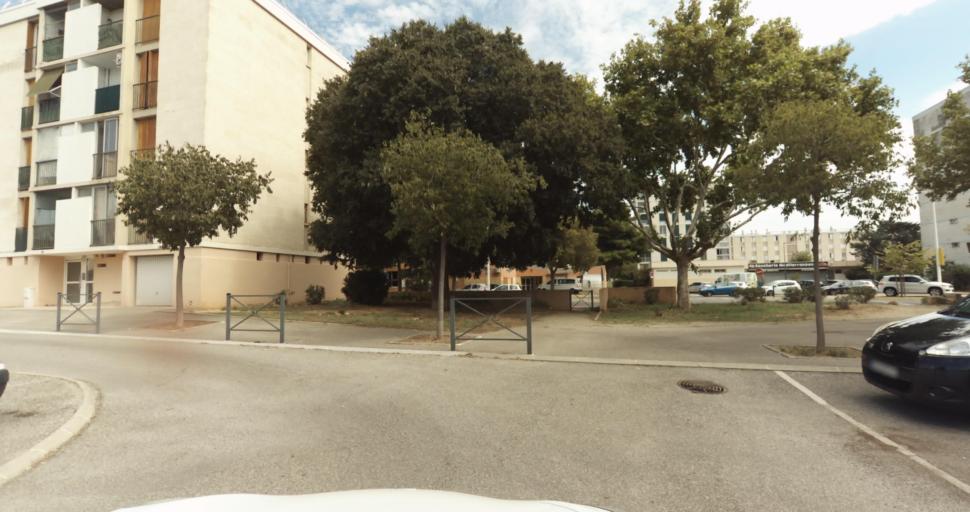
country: FR
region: Provence-Alpes-Cote d'Azur
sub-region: Departement des Bouches-du-Rhone
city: Miramas
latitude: 43.5891
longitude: 5.0047
